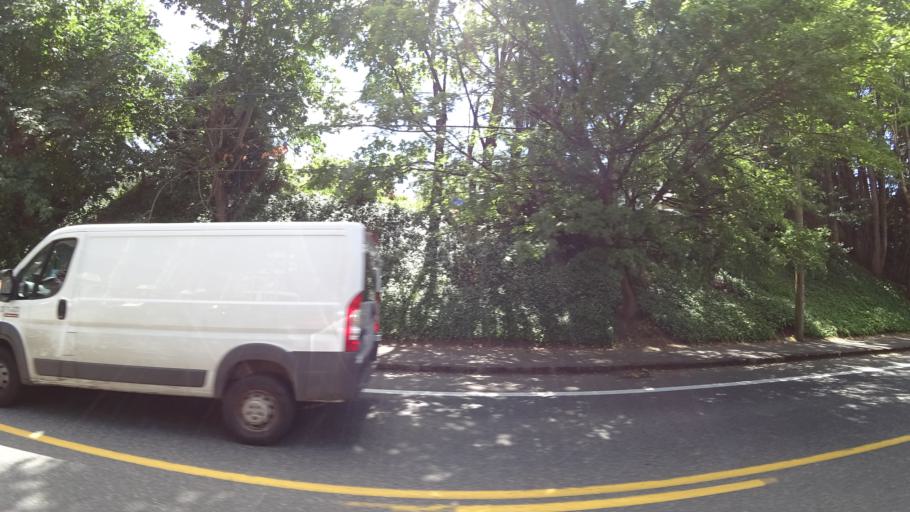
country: US
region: Oregon
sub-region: Multnomah County
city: Portland
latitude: 45.5369
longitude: -122.7088
